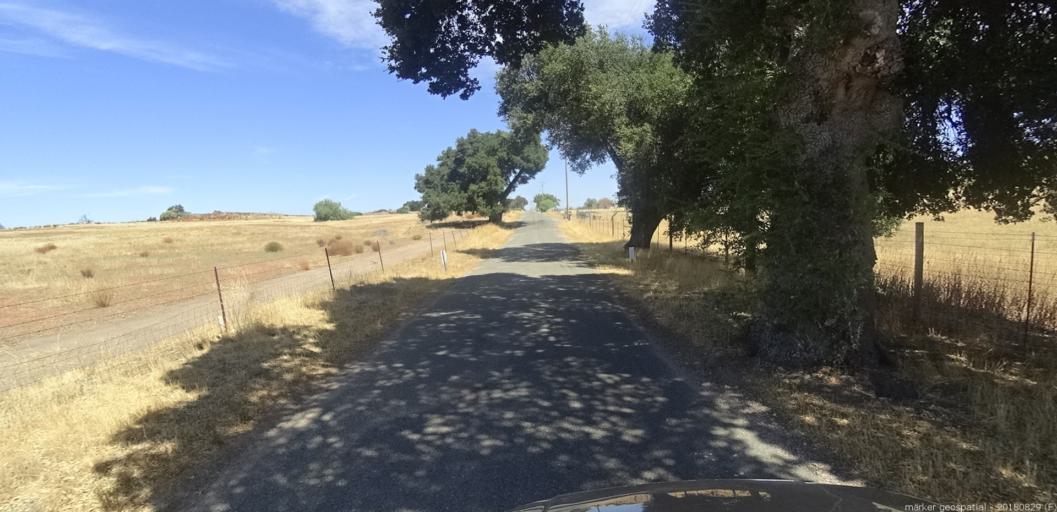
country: US
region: California
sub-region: San Luis Obispo County
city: Lake Nacimiento
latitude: 35.8120
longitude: -121.0574
